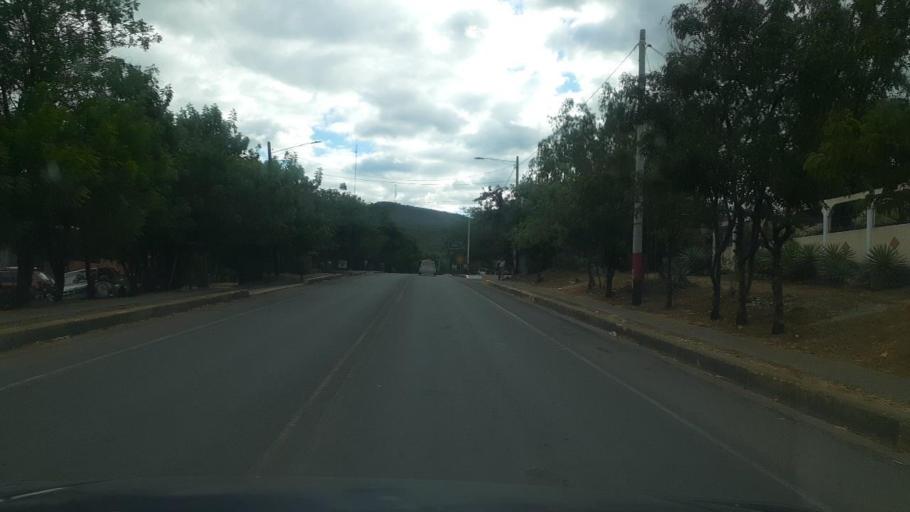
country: NI
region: Madriz
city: Somoto
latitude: 13.4855
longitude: -86.5839
